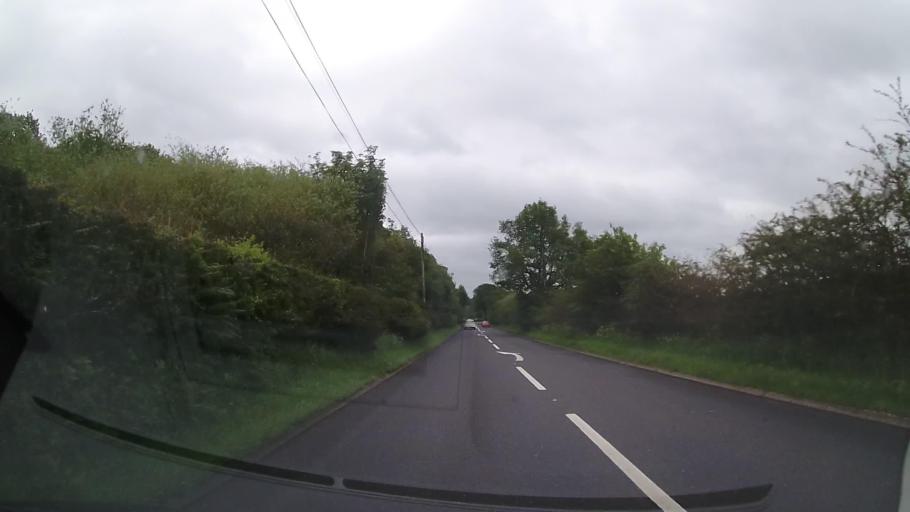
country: GB
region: England
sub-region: Staffordshire
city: Newcastle under Lyme
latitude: 52.9731
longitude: -2.2587
